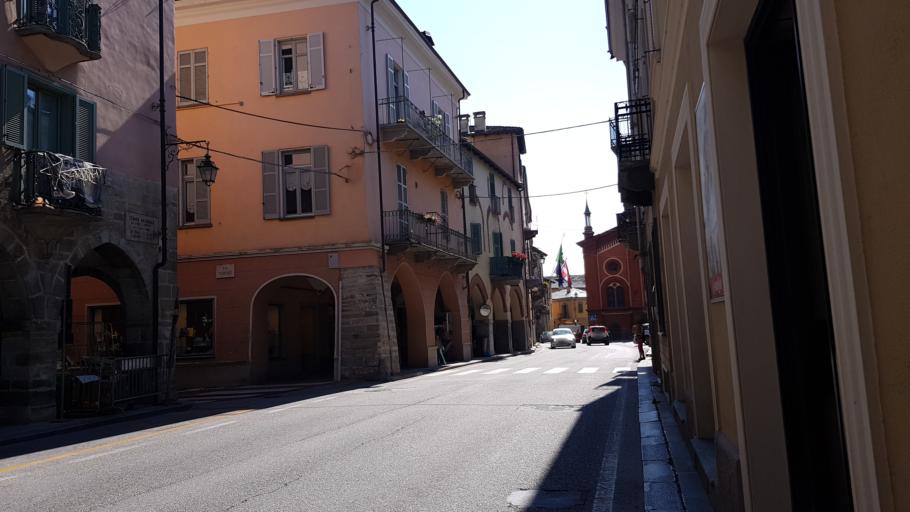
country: IT
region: Piedmont
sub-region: Provincia di Cuneo
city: Dronero
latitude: 44.4676
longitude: 7.3622
